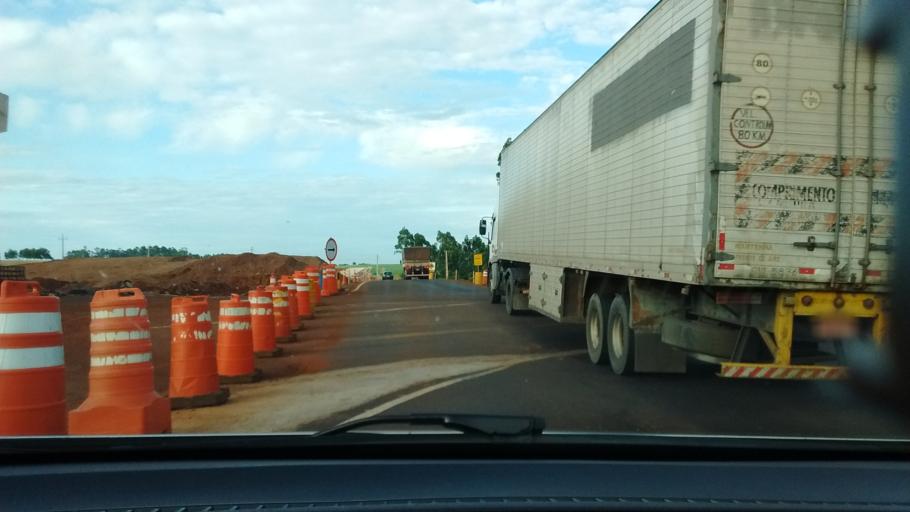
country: BR
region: Parana
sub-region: Cascavel
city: Cascavel
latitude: -25.0799
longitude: -53.5818
